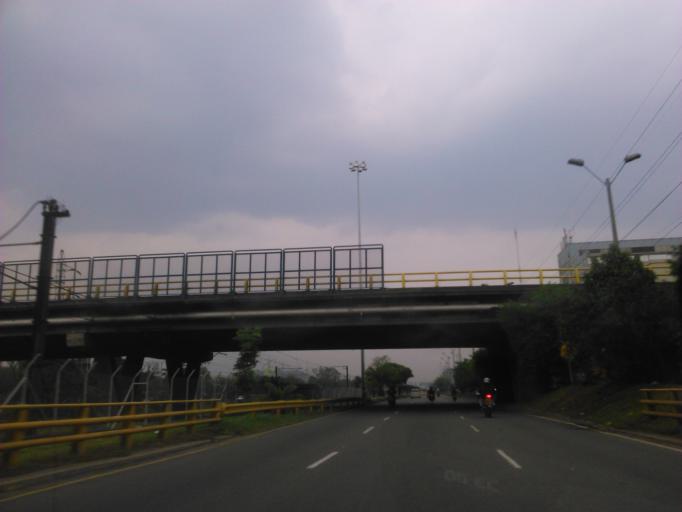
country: CO
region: Antioquia
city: Itagui
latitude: 6.2131
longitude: -75.5778
